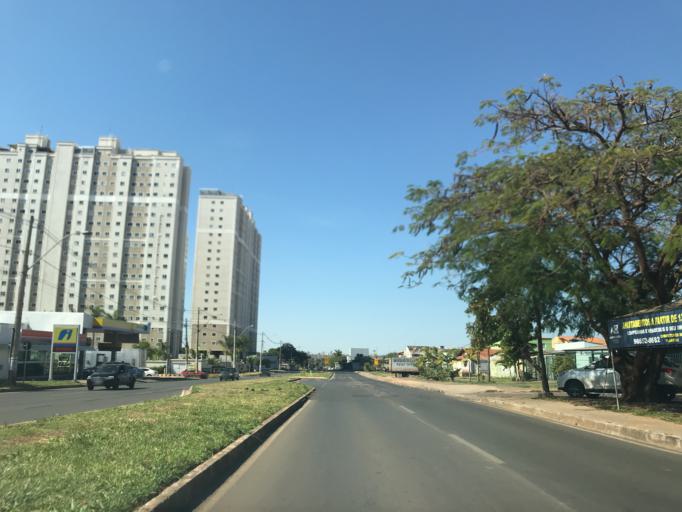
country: BR
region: Federal District
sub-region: Brasilia
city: Brasilia
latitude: -15.8113
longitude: -48.0823
